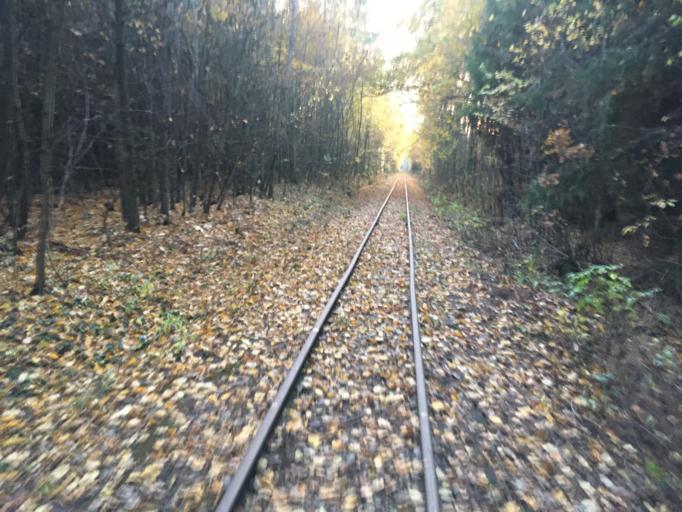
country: PL
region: Swietokrzyskie
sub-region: Powiat starachowicki
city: Starachowice
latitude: 51.0672
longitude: 21.1254
